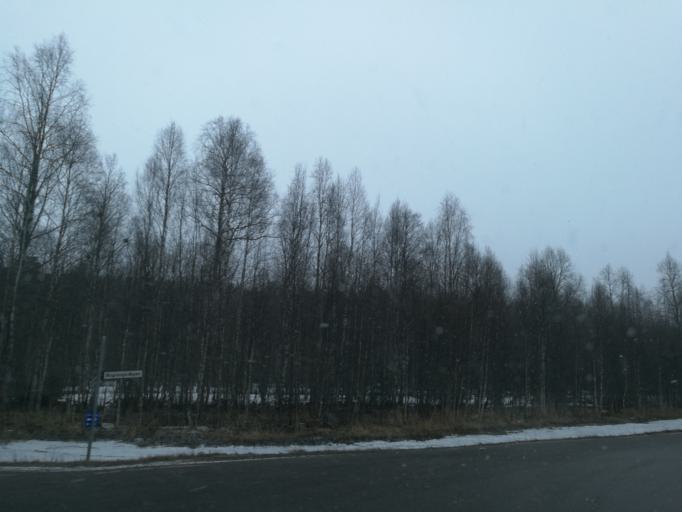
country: NO
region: Hedmark
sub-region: Grue
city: Kirkenaer
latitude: 60.7040
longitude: 12.6144
